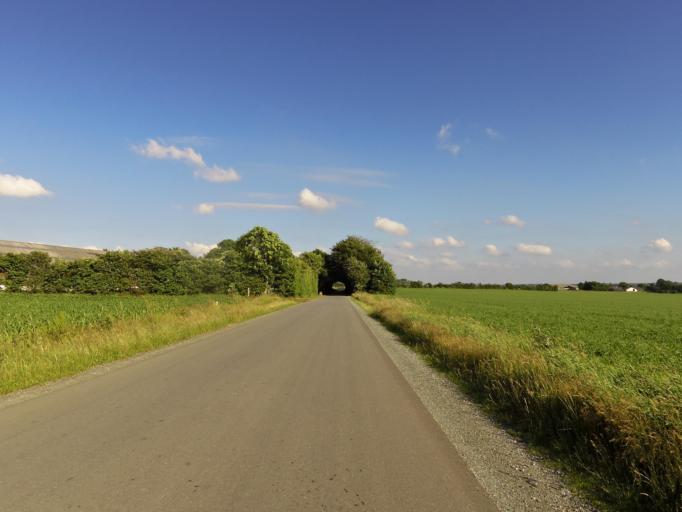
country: DK
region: South Denmark
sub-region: Vejen Kommune
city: Rodding
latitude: 55.3289
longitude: 9.1709
